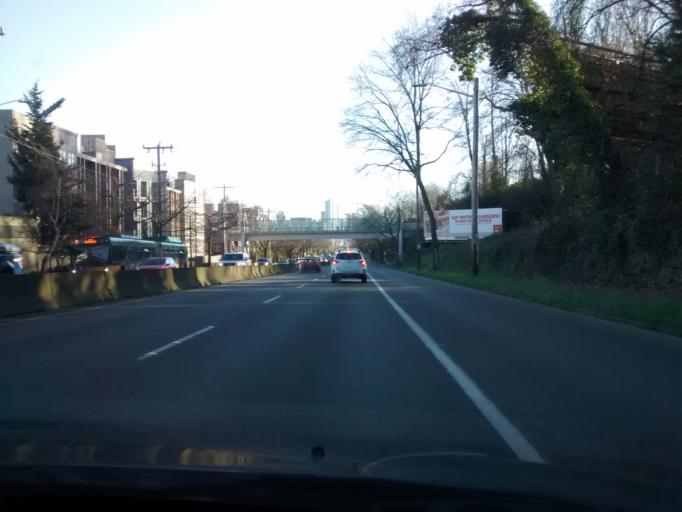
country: US
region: Washington
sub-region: King County
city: Seattle
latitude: 47.6334
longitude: -122.3436
